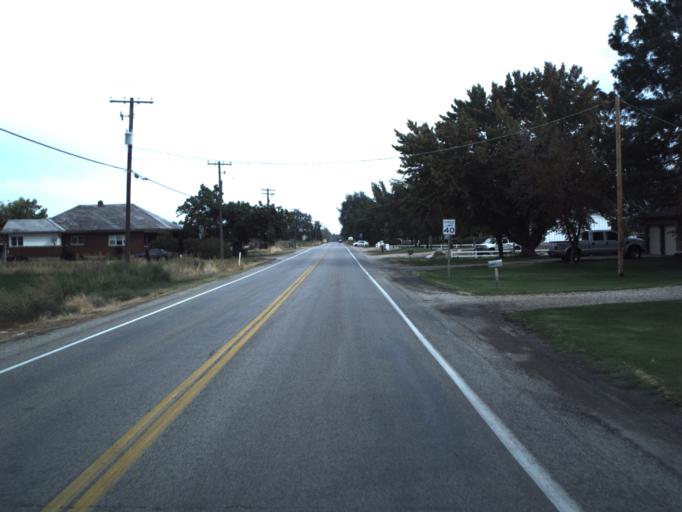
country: US
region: Utah
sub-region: Weber County
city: Plain City
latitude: 41.2610
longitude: -112.0924
